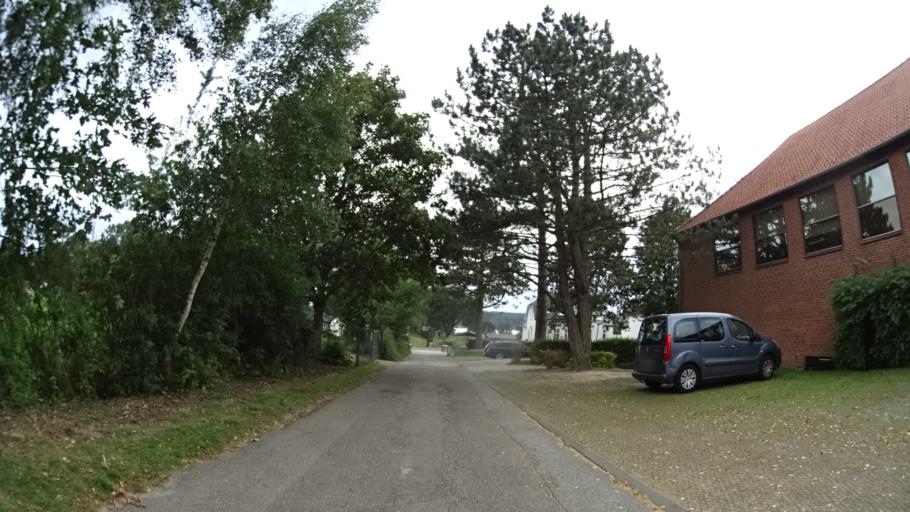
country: DK
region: Central Jutland
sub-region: Arhus Kommune
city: Stavtrup
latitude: 56.1524
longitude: 10.1104
